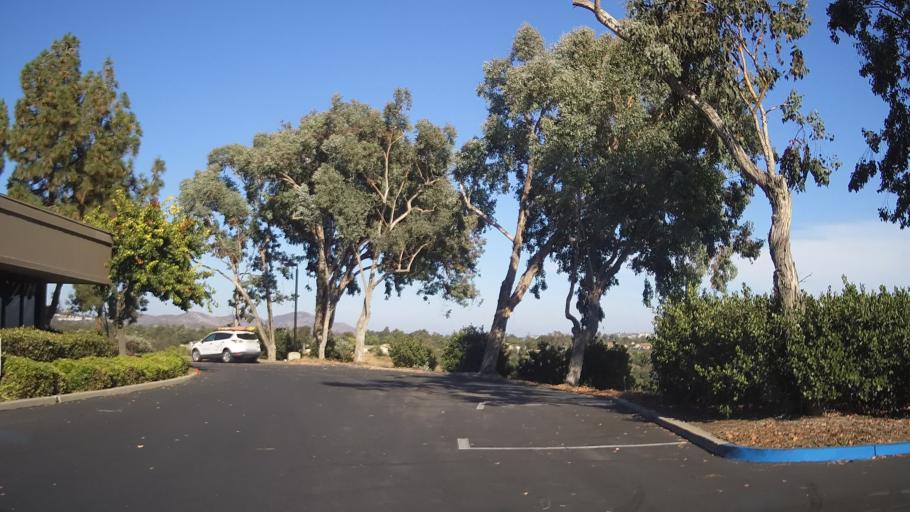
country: US
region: California
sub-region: San Diego County
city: La Mesa
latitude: 32.8210
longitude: -117.1208
